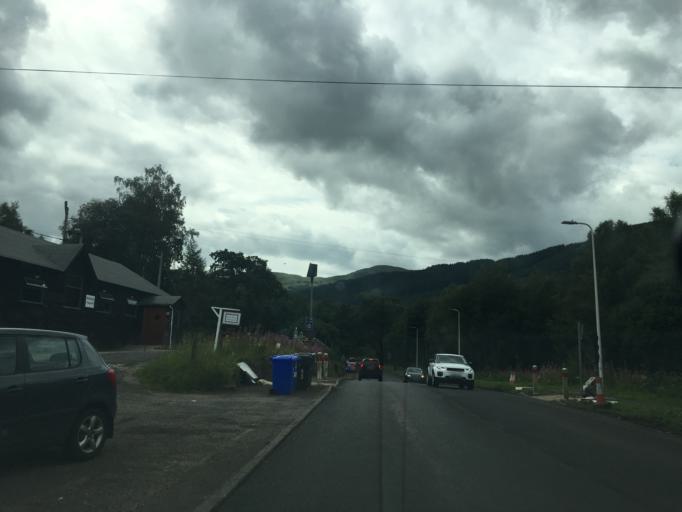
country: GB
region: Scotland
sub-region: Stirling
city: Callander
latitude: 56.3284
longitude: -4.3259
